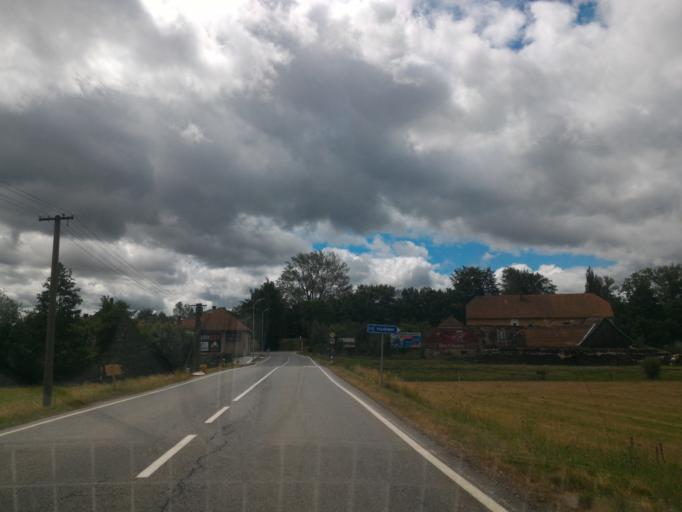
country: CZ
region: Vysocina
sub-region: Okres Jihlava
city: Telc
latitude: 49.1919
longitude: 15.4505
